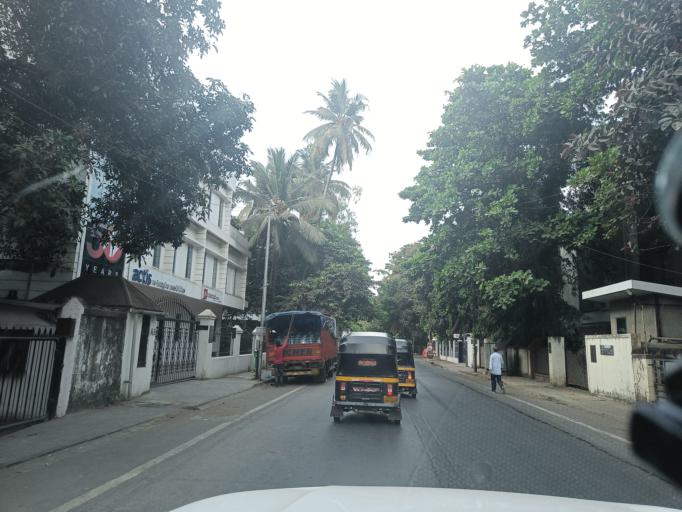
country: IN
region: Maharashtra
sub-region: Mumbai Suburban
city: Powai
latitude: 19.1166
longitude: 72.8683
